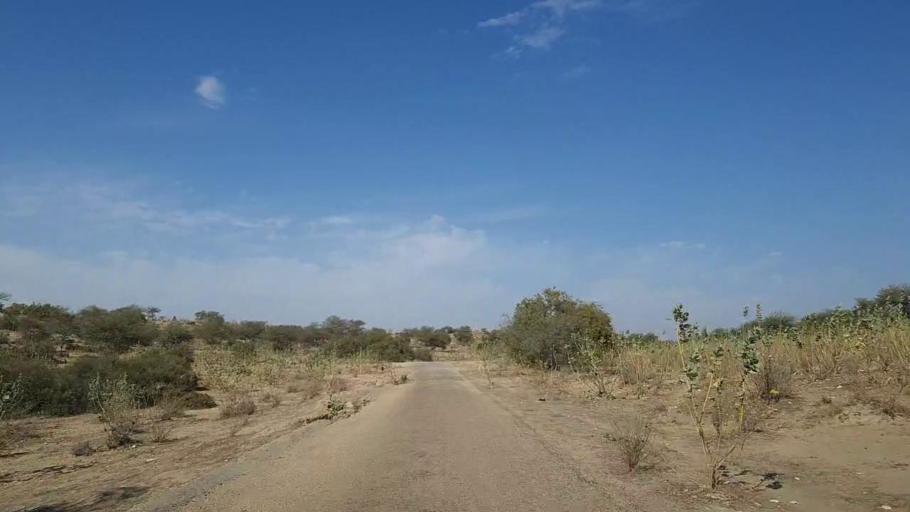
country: PK
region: Sindh
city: Naukot
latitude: 24.8391
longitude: 69.5515
